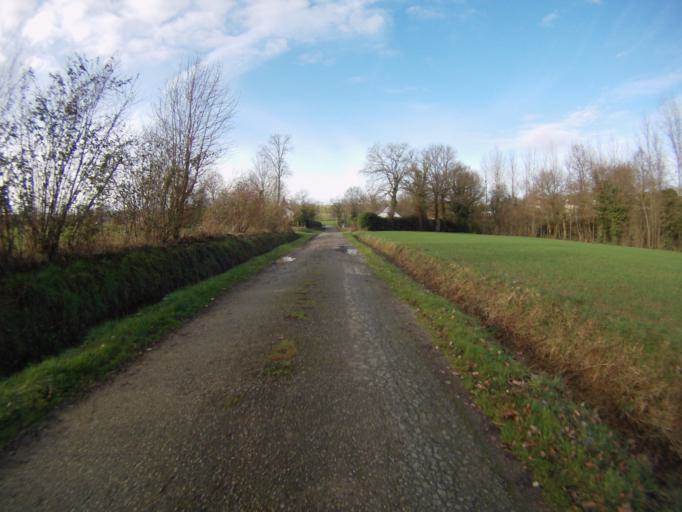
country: FR
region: Brittany
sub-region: Departement d'Ille-et-Vilaine
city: Chanteloup
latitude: 47.9255
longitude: -1.6153
